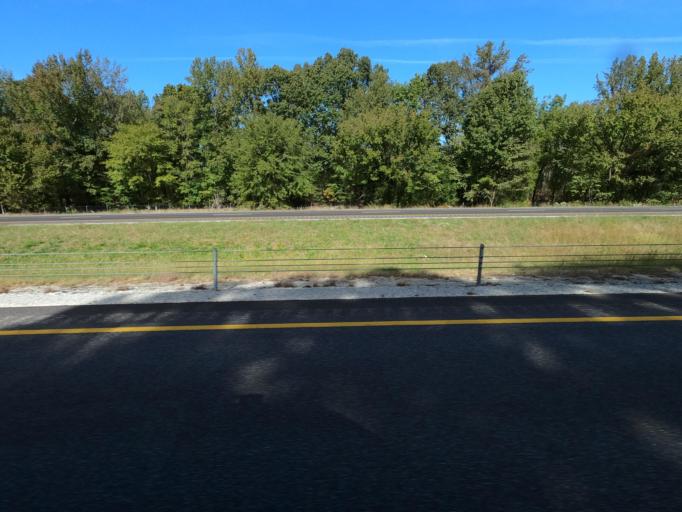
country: US
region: Tennessee
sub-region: Crockett County
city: Bells
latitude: 35.6155
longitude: -89.0049
